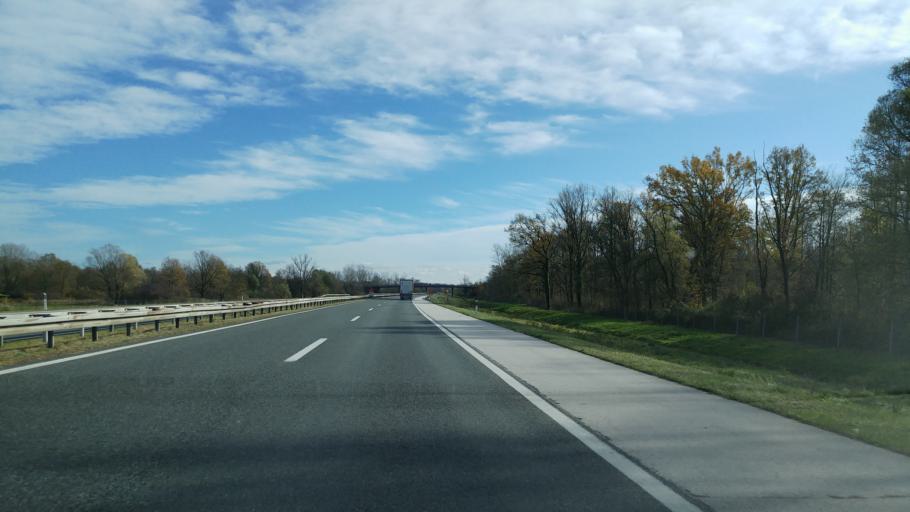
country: HR
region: Sisacko-Moslavacka
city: Husain
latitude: 45.4455
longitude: 16.8136
